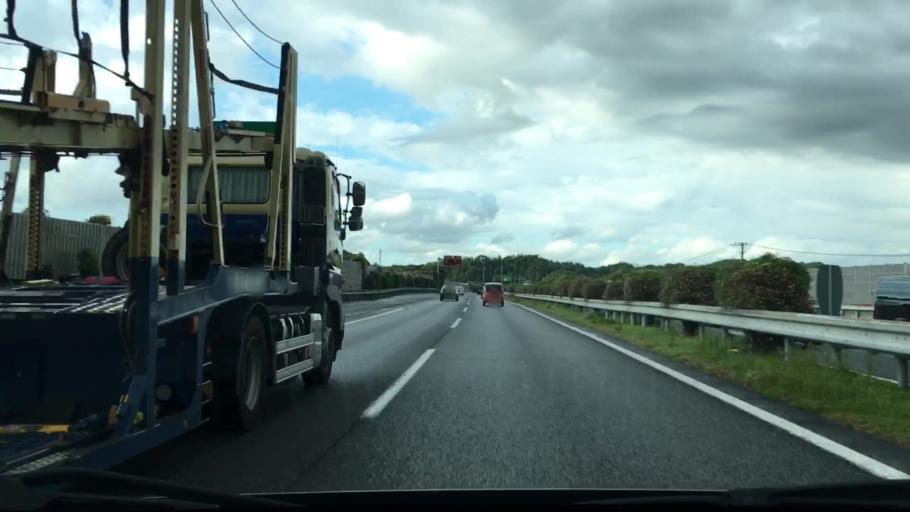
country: JP
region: Fukuoka
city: Koga
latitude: 33.7123
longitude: 130.4896
